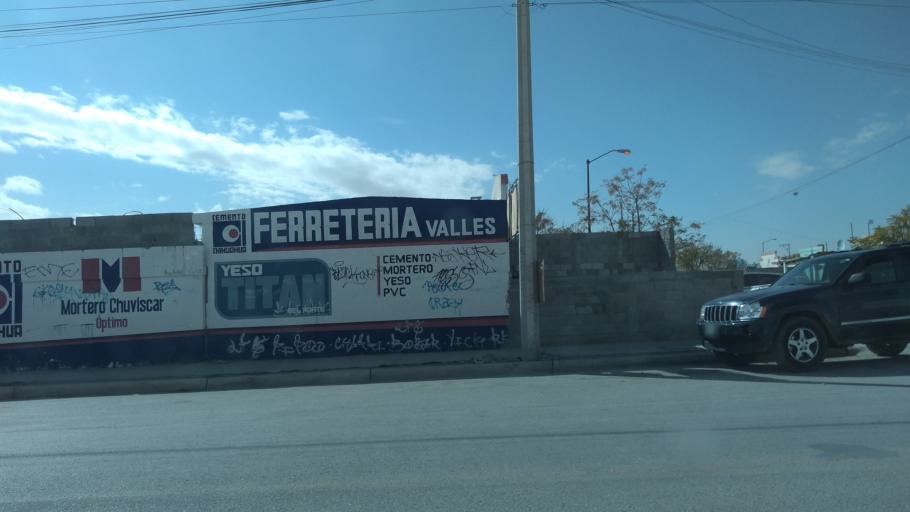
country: US
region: Texas
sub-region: El Paso County
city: San Elizario
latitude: 31.5631
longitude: -106.3357
